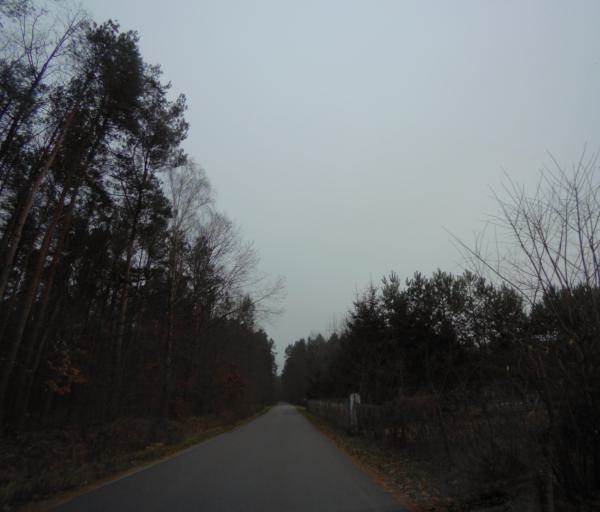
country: PL
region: Subcarpathian Voivodeship
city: Nowa Sarzyna
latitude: 50.3122
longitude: 22.3424
